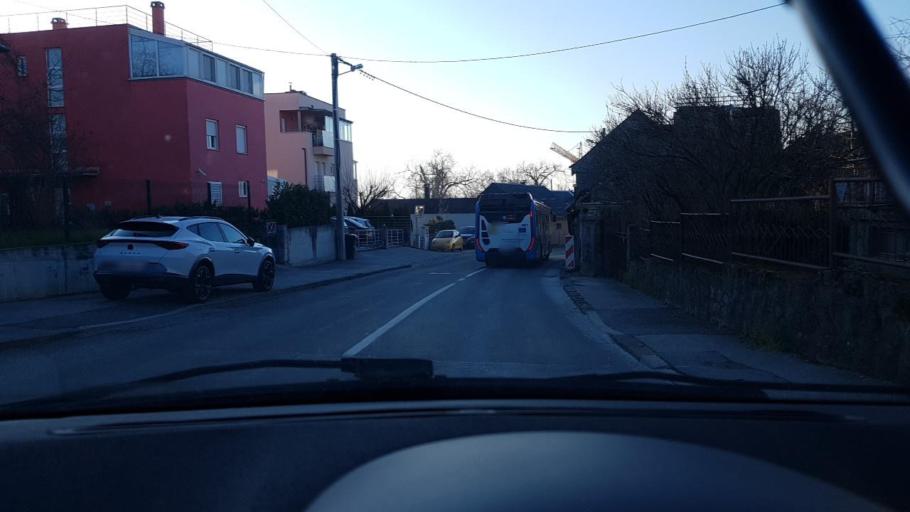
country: HR
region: Grad Zagreb
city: Zagreb
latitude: 45.8475
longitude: 15.9976
